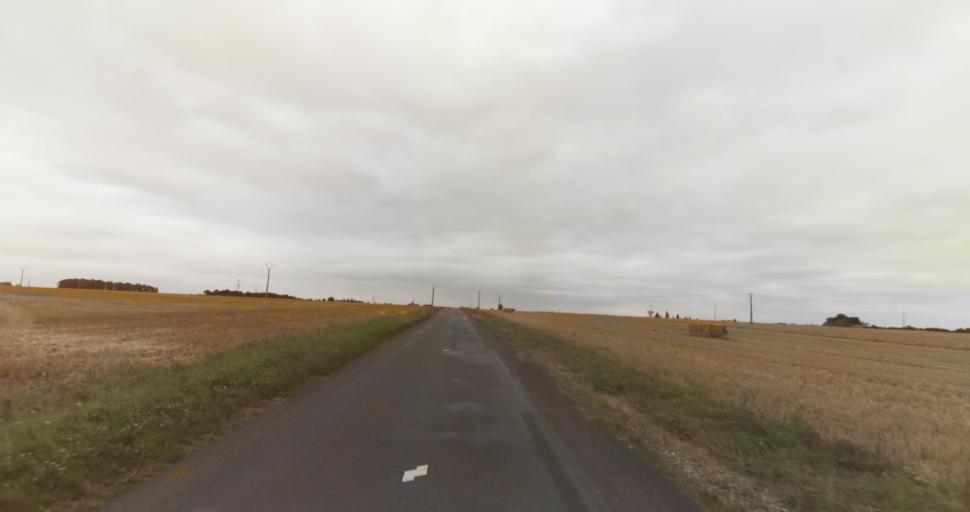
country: FR
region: Haute-Normandie
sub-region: Departement de l'Eure
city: La Couture-Boussey
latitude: 48.9077
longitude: 1.4077
